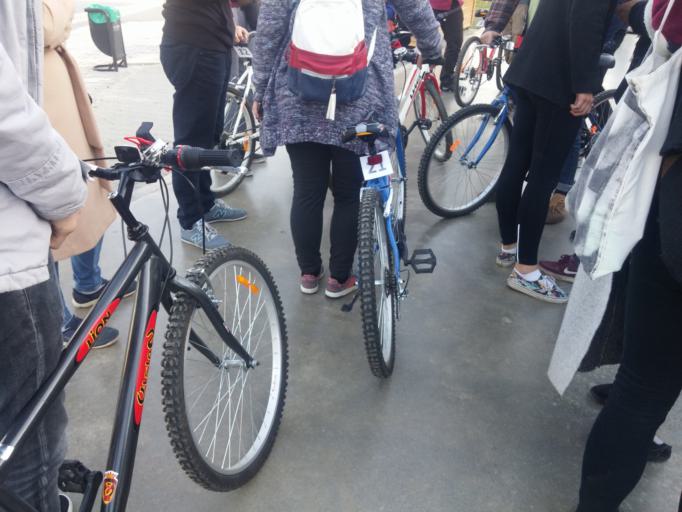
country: TR
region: Izmir
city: Izmir
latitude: 38.4161
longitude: 27.1263
